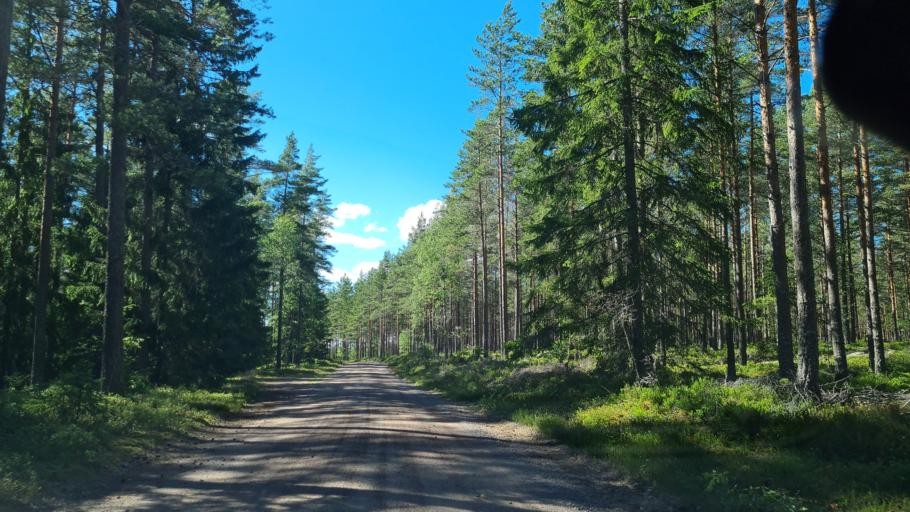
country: SE
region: OEstergoetland
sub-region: Norrkopings Kommun
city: Krokek
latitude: 58.6926
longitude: 16.4317
